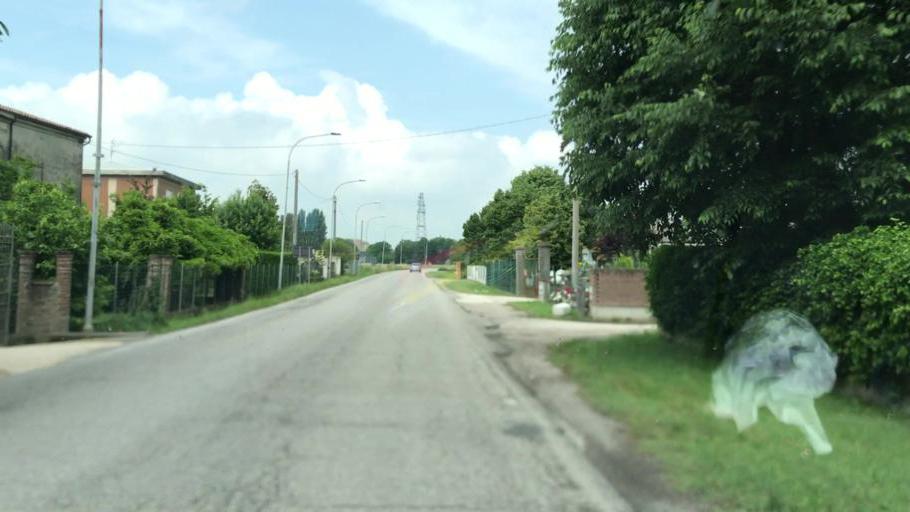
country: IT
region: Lombardy
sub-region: Provincia di Mantova
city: Poggio Rusco
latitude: 44.9772
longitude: 11.1121
